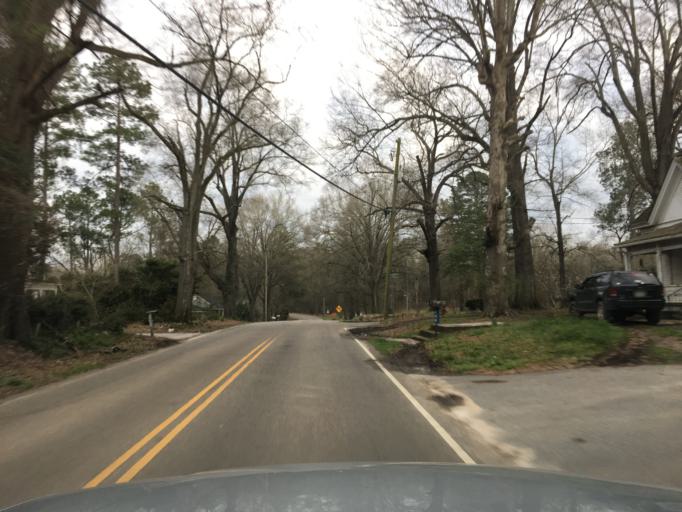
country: US
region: South Carolina
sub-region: Saluda County
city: Saluda
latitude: 33.9965
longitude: -81.7726
